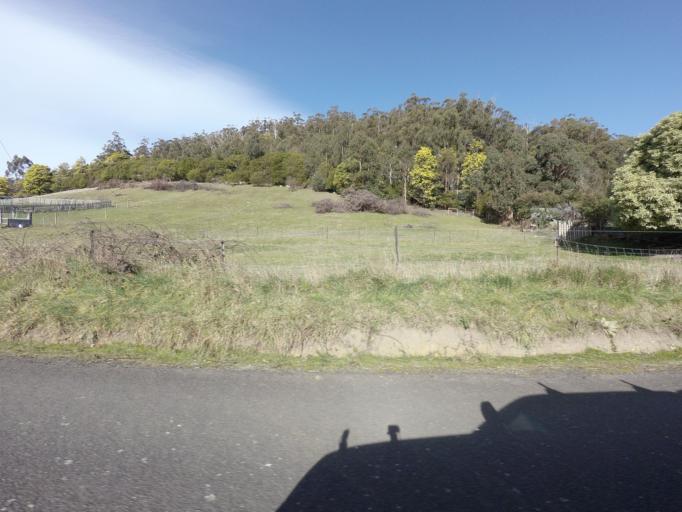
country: AU
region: Tasmania
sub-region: Huon Valley
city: Cygnet
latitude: -43.1750
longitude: 147.1546
